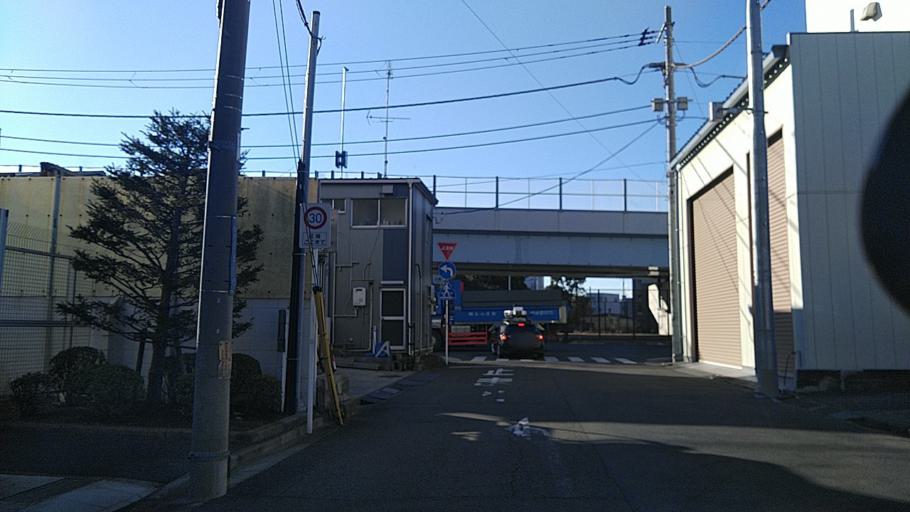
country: JP
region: Kanagawa
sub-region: Kawasaki-shi
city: Kawasaki
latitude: 35.5379
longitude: 139.7501
